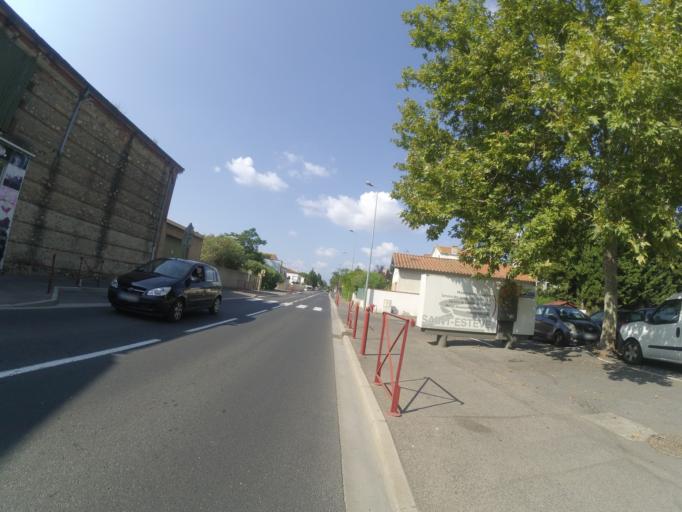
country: FR
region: Languedoc-Roussillon
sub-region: Departement des Pyrenees-Orientales
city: Saint-Esteve
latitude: 42.7086
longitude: 2.8432
